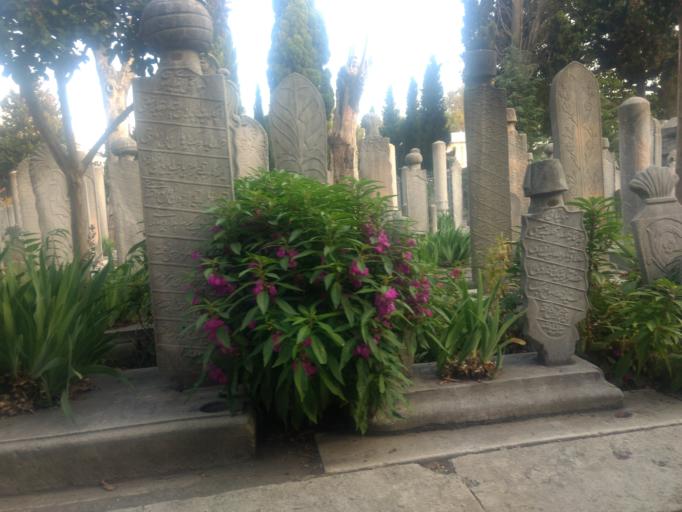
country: TR
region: Istanbul
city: Eminoenue
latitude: 41.0157
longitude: 28.9642
